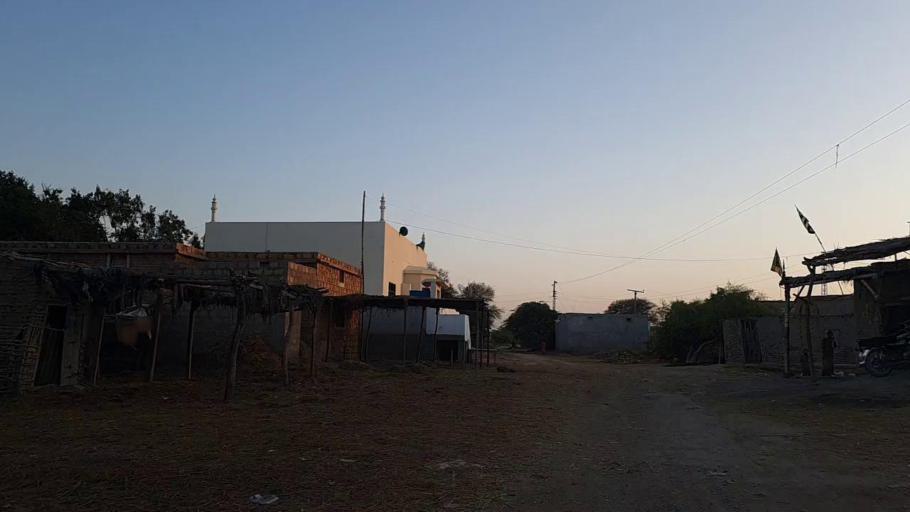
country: PK
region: Sindh
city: Mirpur Batoro
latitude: 24.6449
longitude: 68.1899
